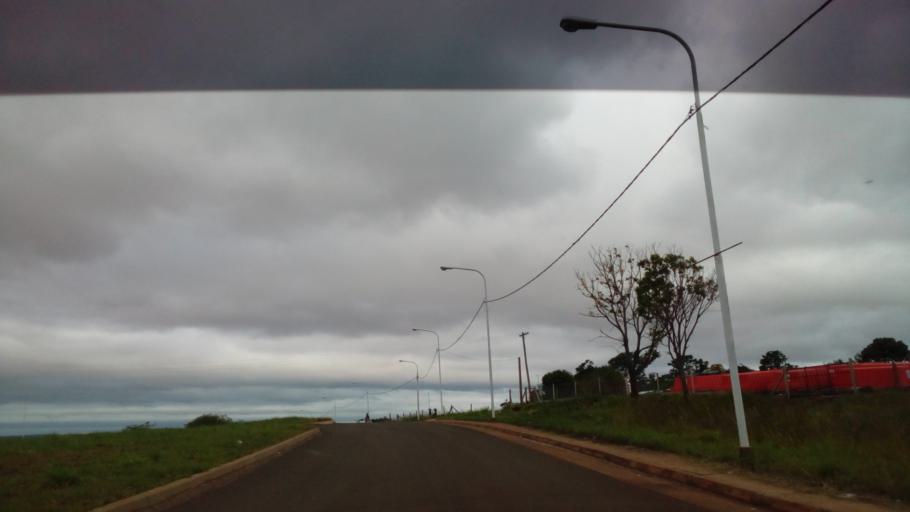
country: AR
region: Misiones
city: Garupa
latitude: -27.4518
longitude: -55.8568
